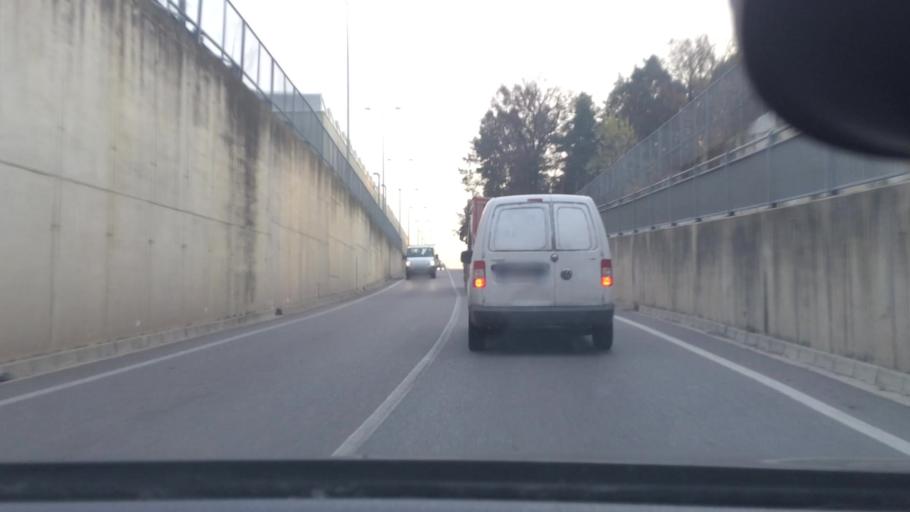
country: IT
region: Lombardy
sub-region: Provincia di Monza e Brianza
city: Villaggio del Sole
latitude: 45.6271
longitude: 9.1015
